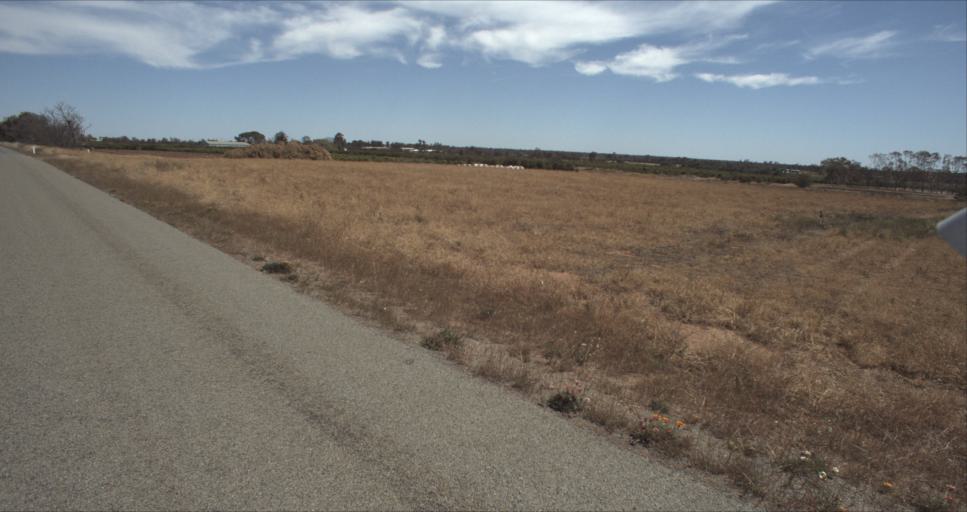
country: AU
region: New South Wales
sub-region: Leeton
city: Leeton
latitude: -34.6094
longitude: 146.4348
